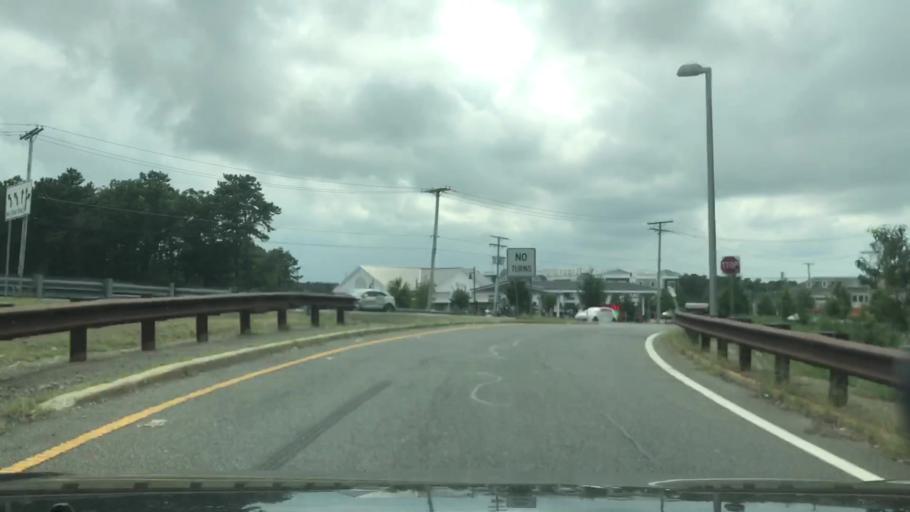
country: US
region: New Jersey
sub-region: Ocean County
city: Barnegat
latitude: 39.7600
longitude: -74.2523
